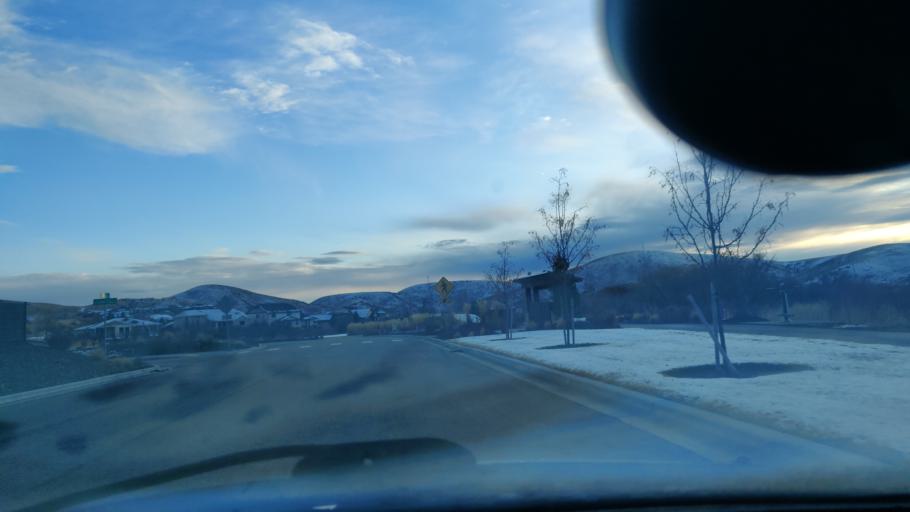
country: US
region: Idaho
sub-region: Ada County
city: Eagle
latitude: 43.7783
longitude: -116.2624
